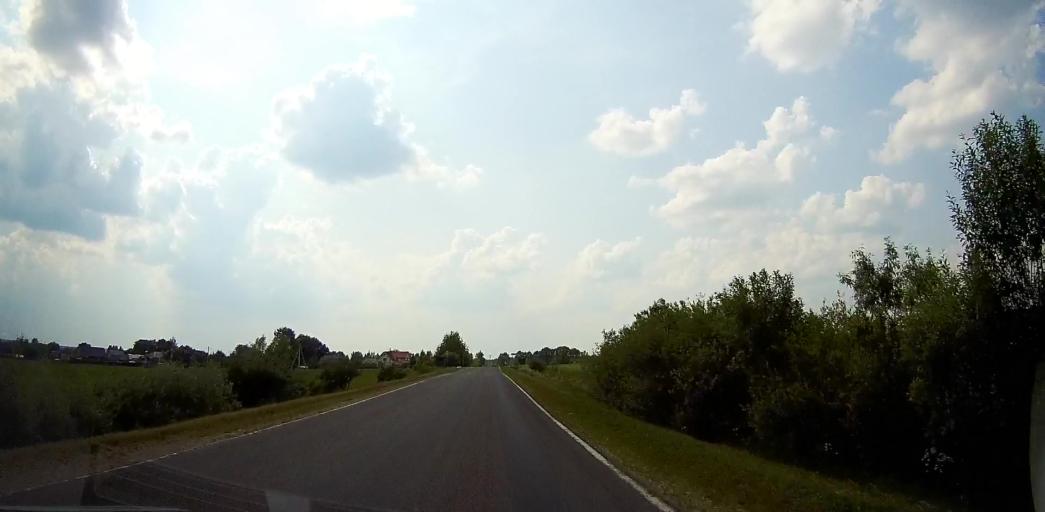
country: RU
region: Moskovskaya
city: Malino
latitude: 55.0644
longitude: 38.1113
